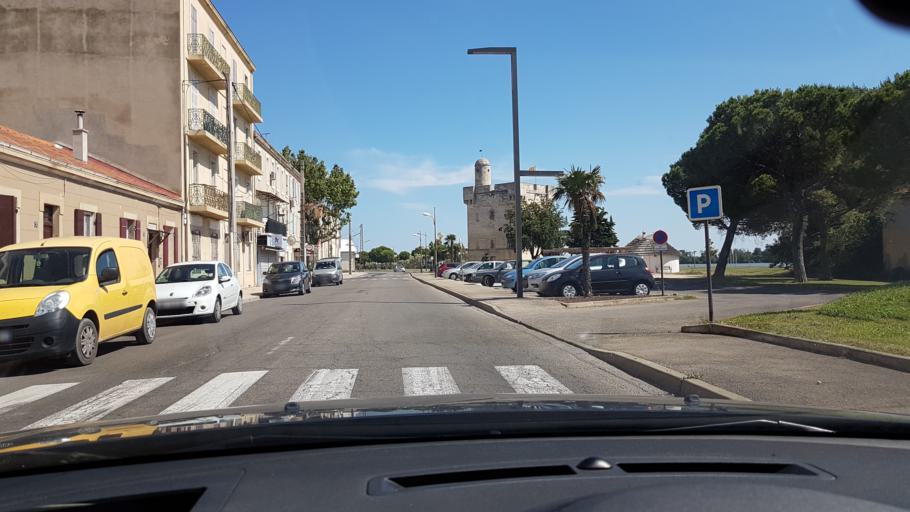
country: FR
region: Provence-Alpes-Cote d'Azur
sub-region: Departement des Bouches-du-Rhone
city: Port-Saint-Louis-du-Rhone
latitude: 43.3857
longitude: 4.8043
